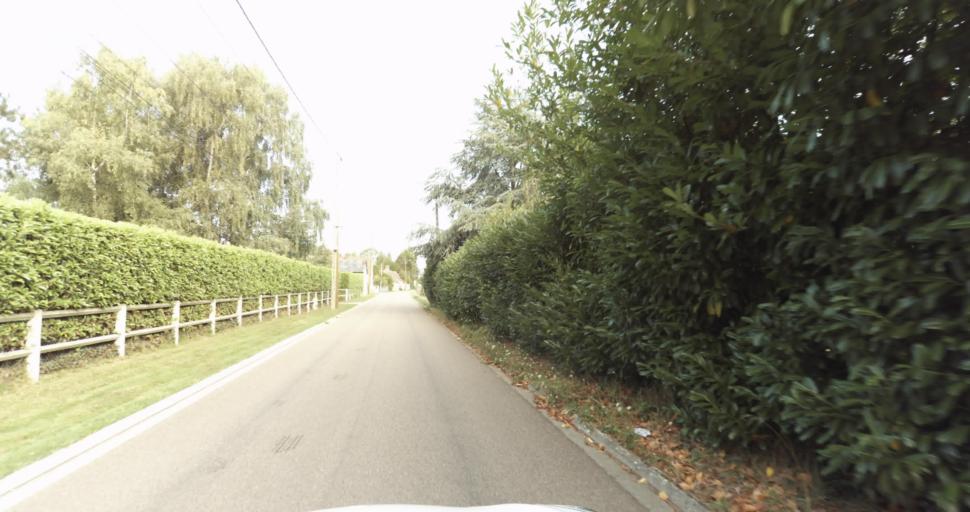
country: FR
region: Haute-Normandie
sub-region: Departement de l'Eure
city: La Madeleine-de-Nonancourt
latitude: 48.8257
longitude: 1.1815
